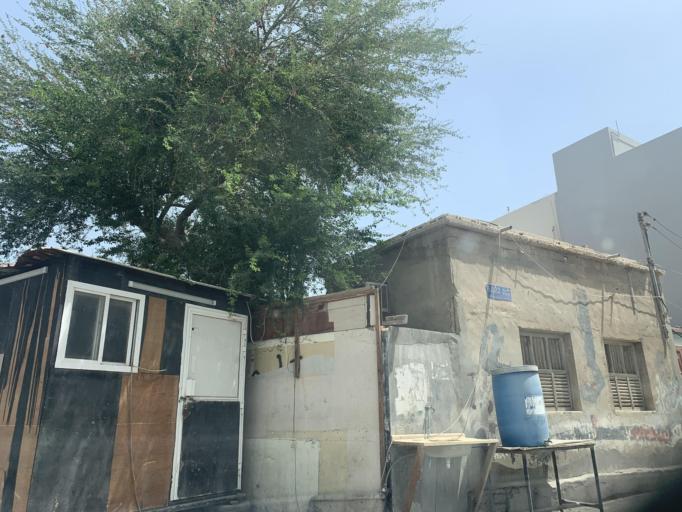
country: BH
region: Manama
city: Jidd Hafs
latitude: 26.2033
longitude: 50.5362
